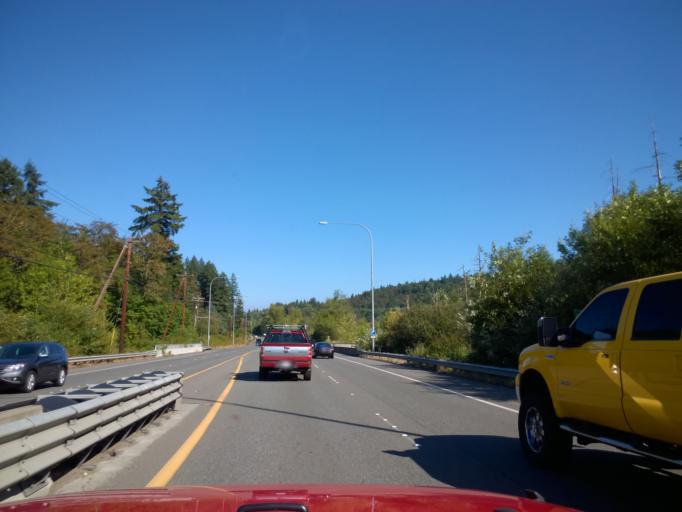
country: US
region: Washington
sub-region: King County
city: Sammamish
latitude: 47.6559
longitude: -122.0795
